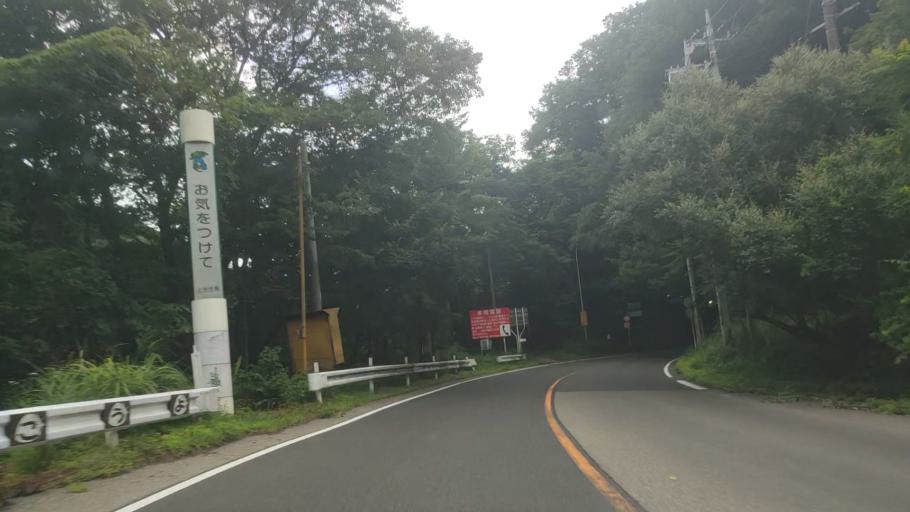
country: JP
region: Gunma
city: Omamacho-omama
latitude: 36.6052
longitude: 139.4060
